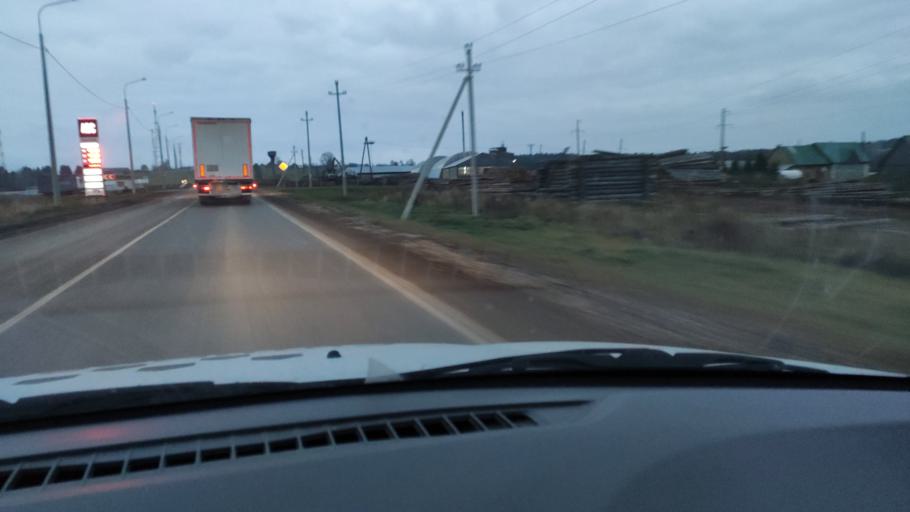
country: RU
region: Kirov
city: Kostino
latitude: 58.8512
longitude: 53.2699
